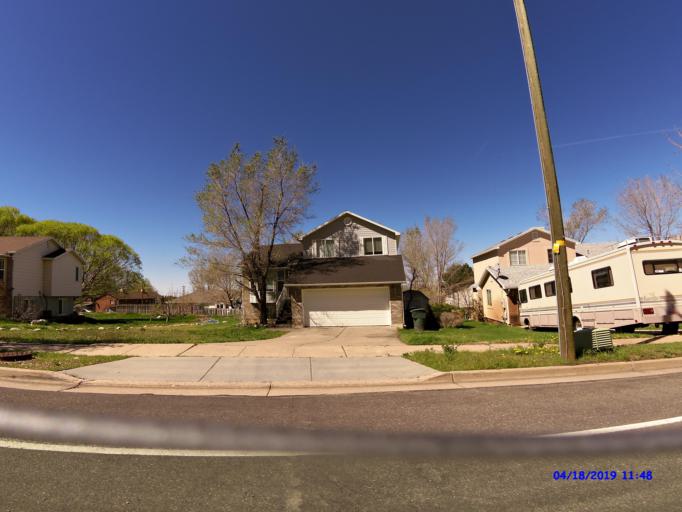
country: US
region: Utah
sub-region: Weber County
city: North Ogden
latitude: 41.2734
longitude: -111.9510
